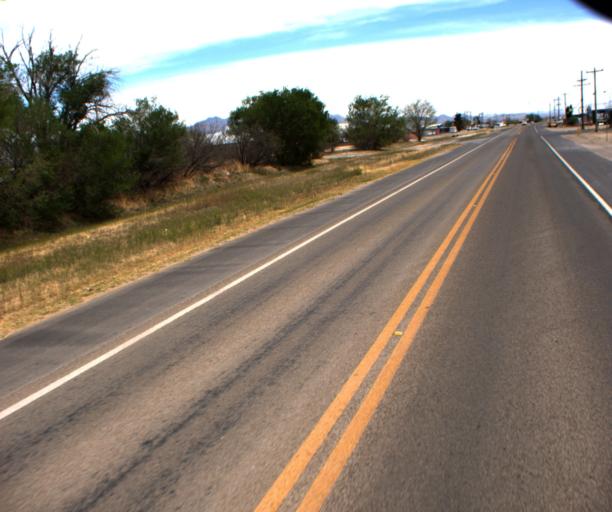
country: US
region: Arizona
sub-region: Cochise County
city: Willcox
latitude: 32.2493
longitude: -109.8258
